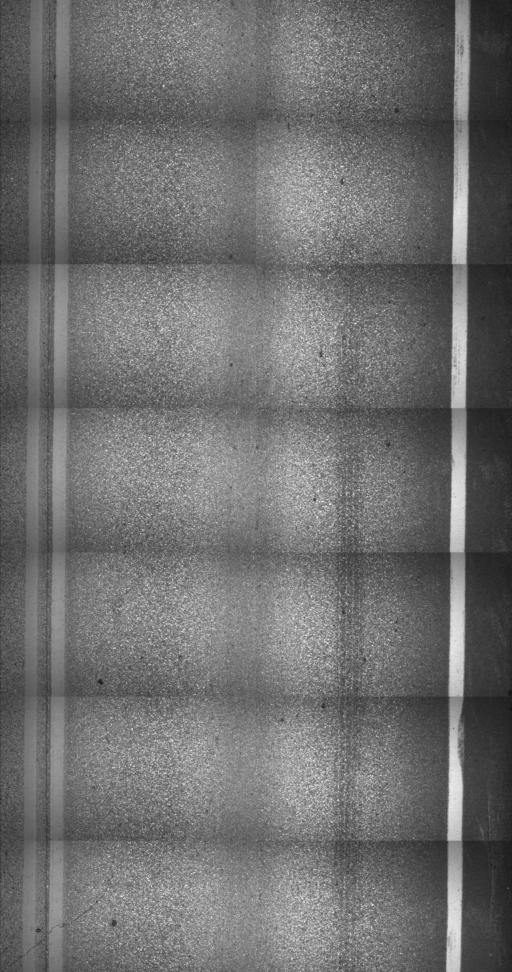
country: US
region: Vermont
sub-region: Rutland County
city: Poultney
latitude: 43.5492
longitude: -73.2267
